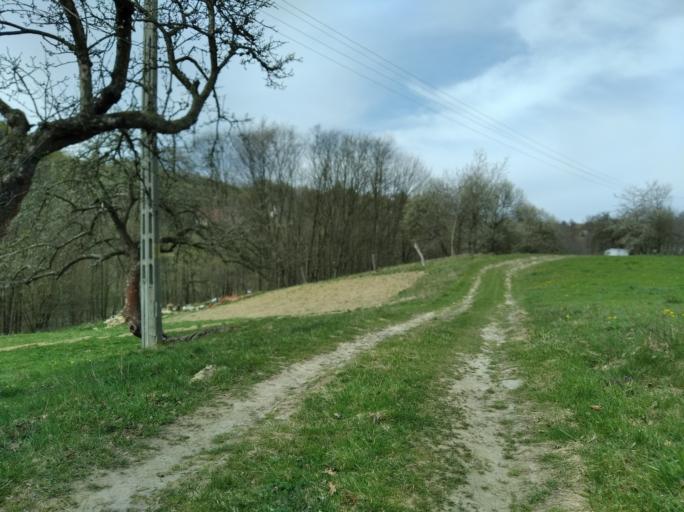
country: PL
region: Subcarpathian Voivodeship
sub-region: Powiat ropczycko-sedziszowski
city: Wielopole Skrzynskie
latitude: 49.9102
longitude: 21.6122
